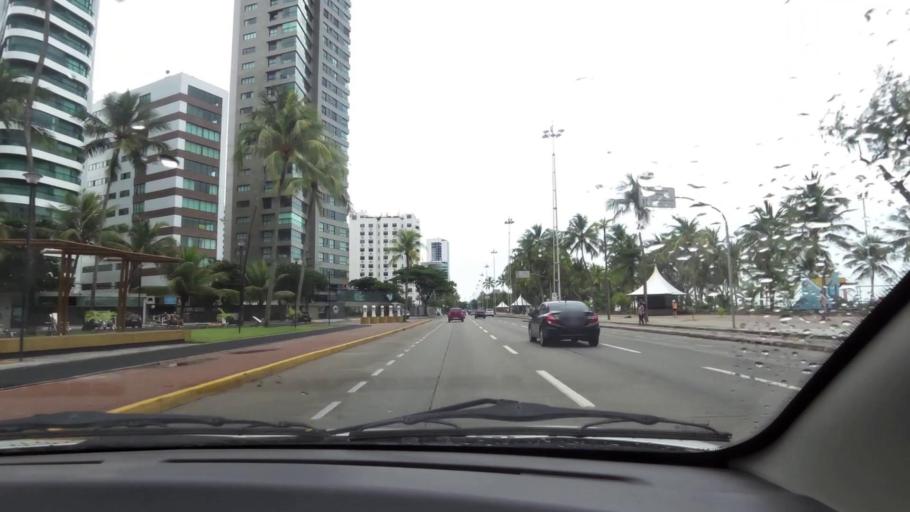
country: BR
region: Pernambuco
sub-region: Recife
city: Recife
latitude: -8.1044
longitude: -34.8867
